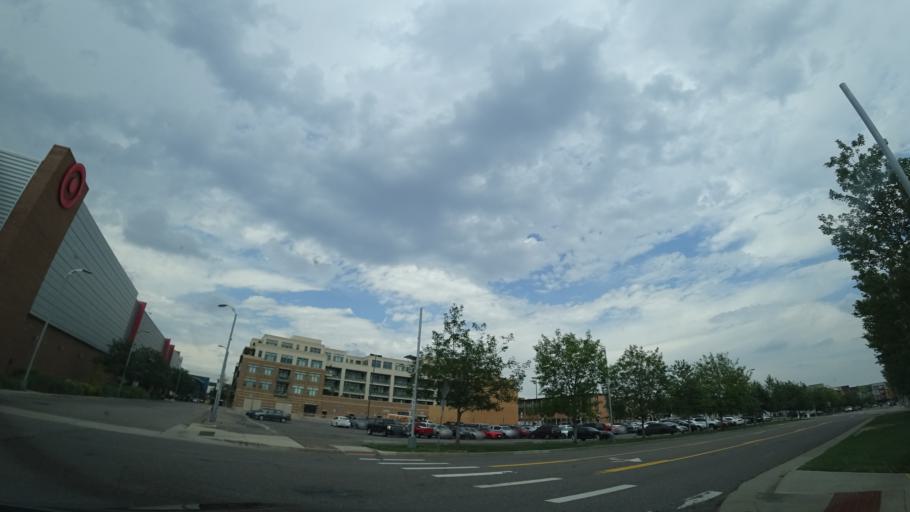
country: US
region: Colorado
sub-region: Jefferson County
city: Lakewood
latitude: 39.7070
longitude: -105.0782
